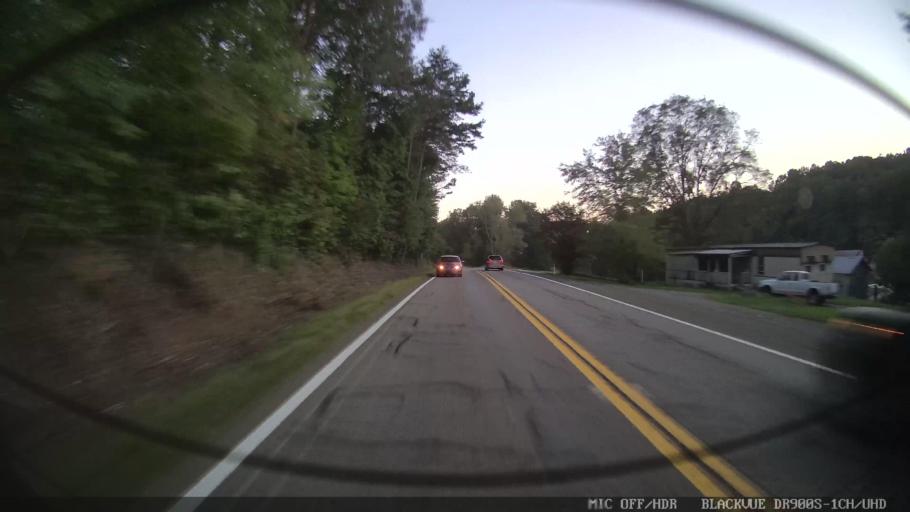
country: US
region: Georgia
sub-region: Gilmer County
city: Ellijay
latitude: 34.7182
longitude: -84.5026
